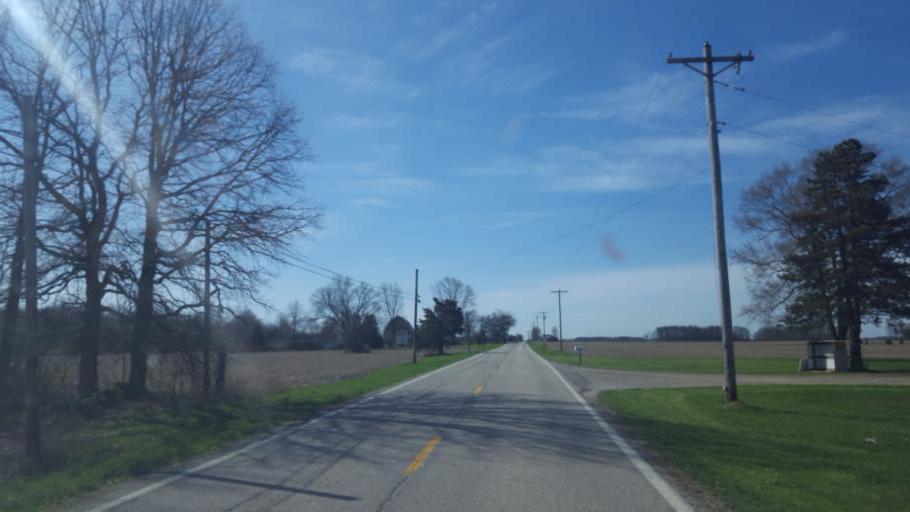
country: US
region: Ohio
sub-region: Morrow County
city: Cardington
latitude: 40.5327
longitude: -82.9626
